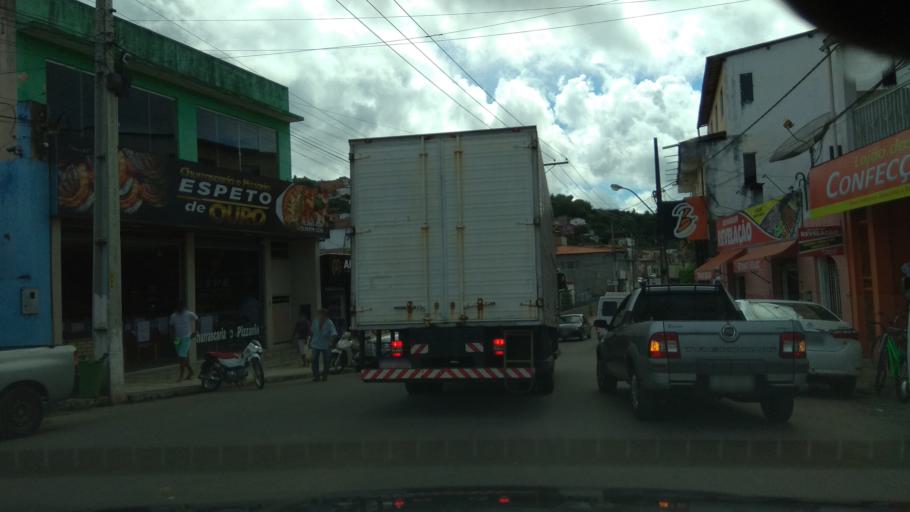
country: BR
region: Bahia
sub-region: Mutuipe
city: Mutuipe
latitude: -13.1830
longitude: -39.4223
